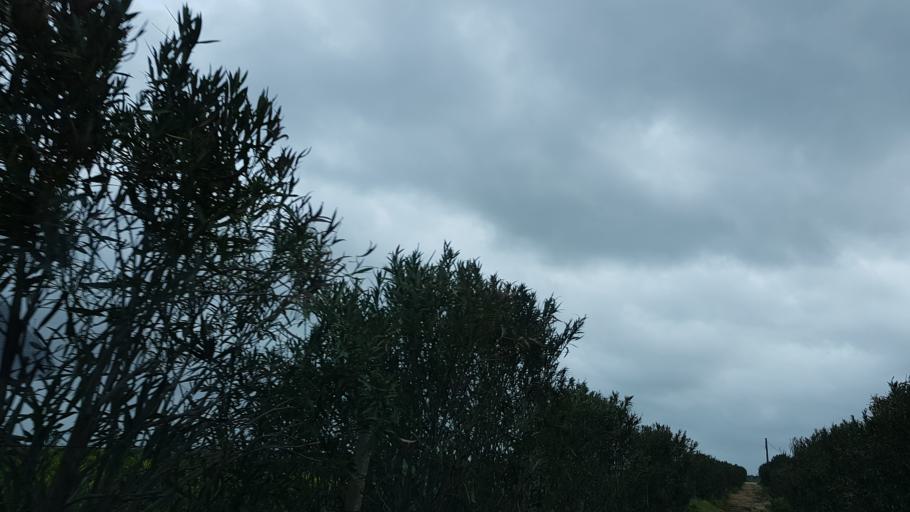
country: IT
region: Apulia
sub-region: Provincia di Brindisi
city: Brindisi
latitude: 40.6565
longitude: 17.8634
